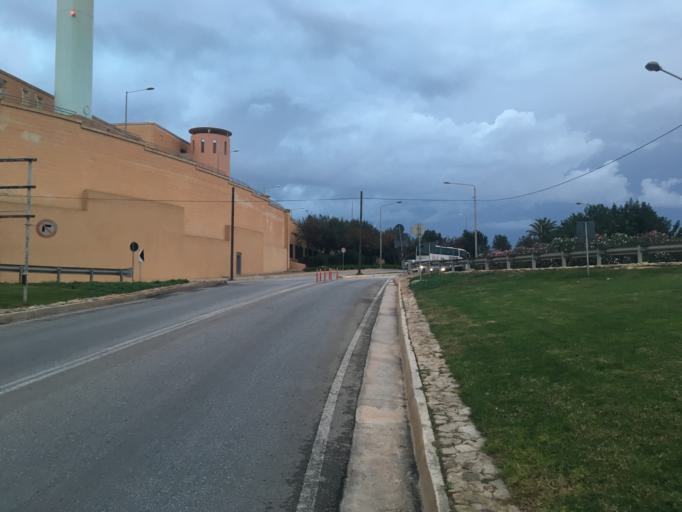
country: MT
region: Saint John
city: Saint John
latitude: 35.9006
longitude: 14.4795
